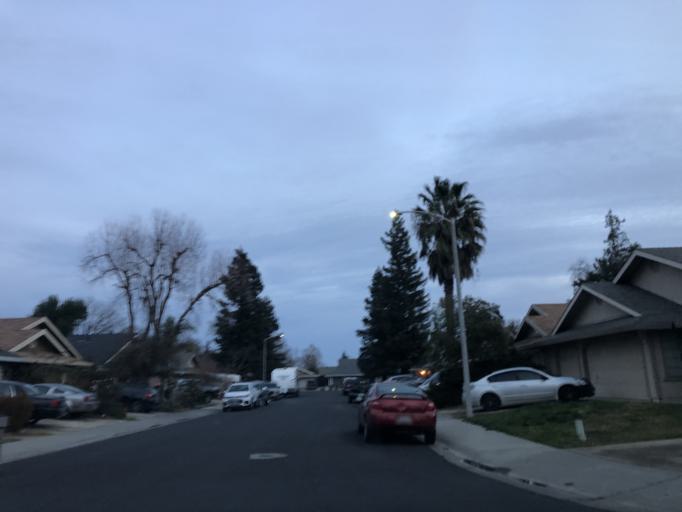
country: US
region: California
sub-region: Yolo County
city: Woodland
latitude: 38.6602
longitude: -121.7606
